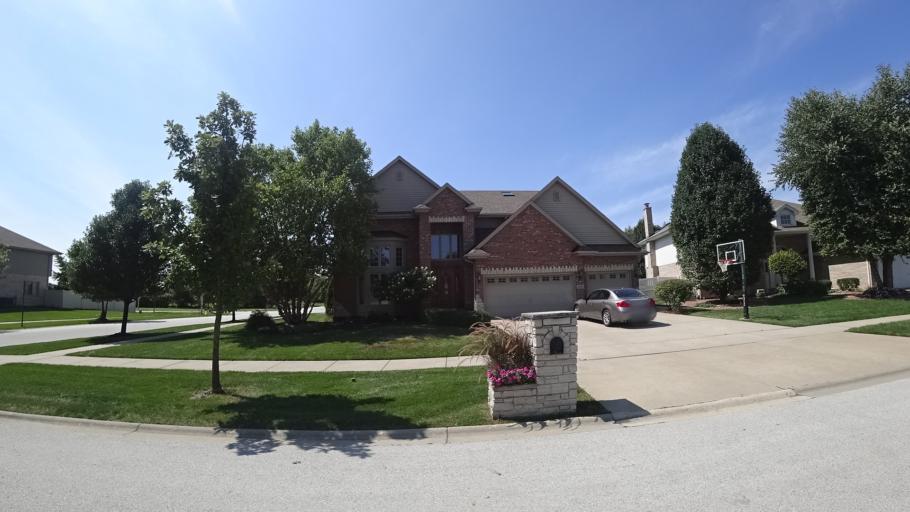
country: US
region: Illinois
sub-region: Cook County
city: Orland Hills
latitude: 41.5611
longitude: -87.8311
